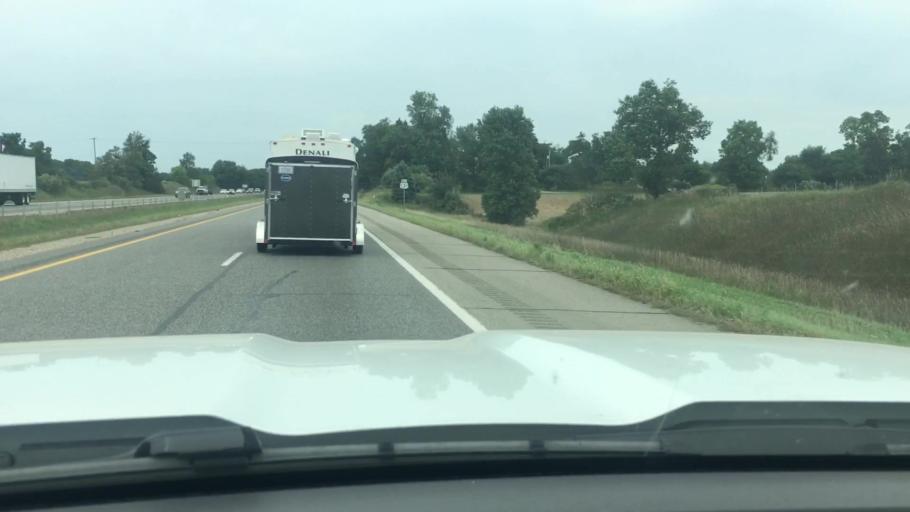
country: US
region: Michigan
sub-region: Allegan County
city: Otsego
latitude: 42.5423
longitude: -85.6610
